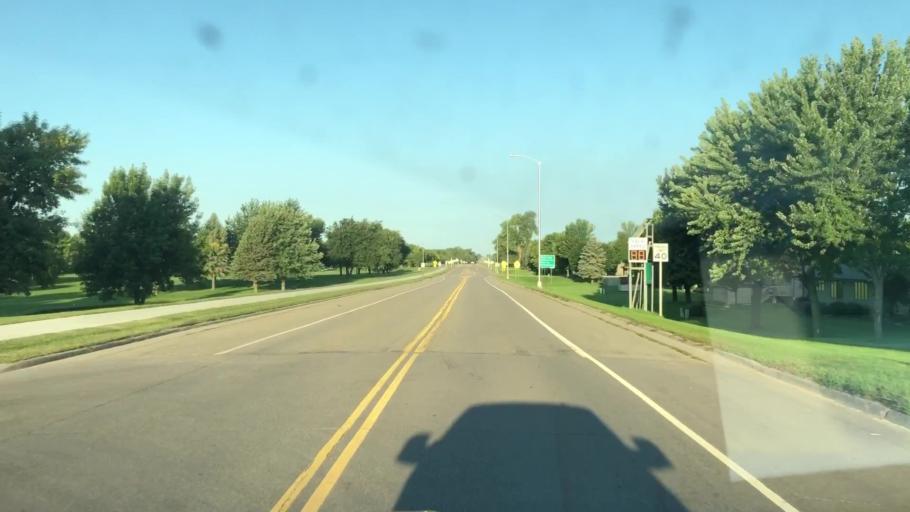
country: US
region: Minnesota
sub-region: Nobles County
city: Worthington
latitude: 43.6310
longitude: -95.6236
